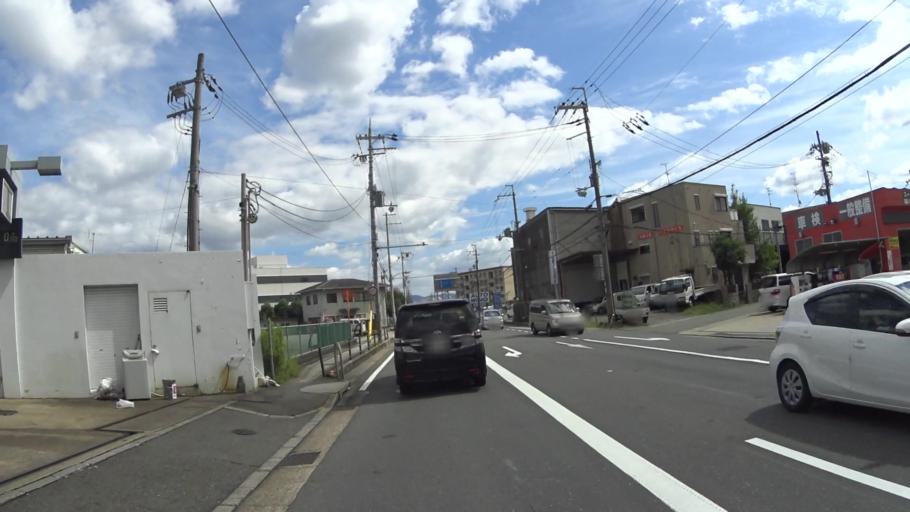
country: JP
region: Kyoto
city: Yawata
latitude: 34.8804
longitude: 135.7363
